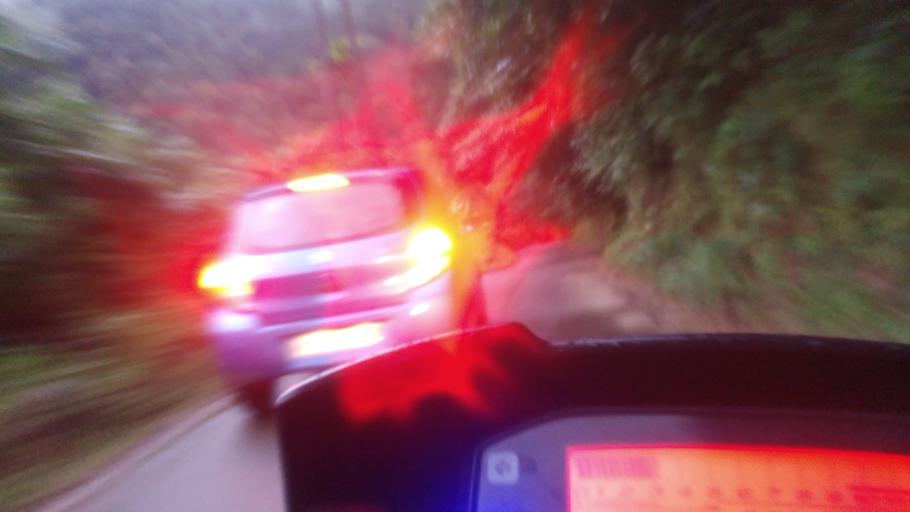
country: IN
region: Kerala
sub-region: Kottayam
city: Erattupetta
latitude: 9.5468
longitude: 76.9711
